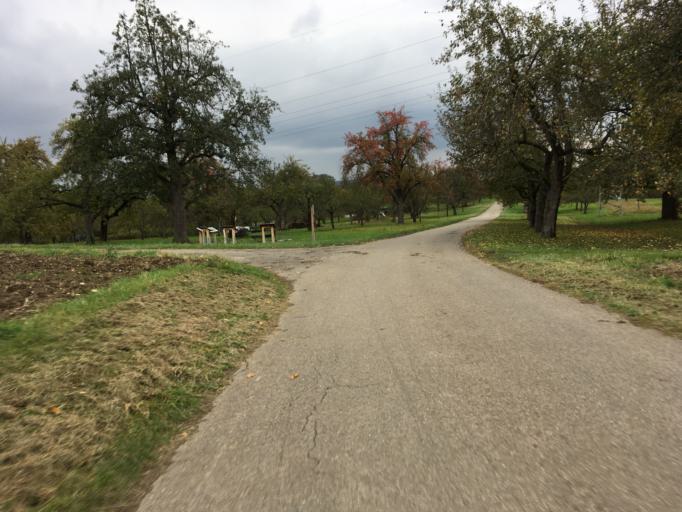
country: DE
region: Baden-Wuerttemberg
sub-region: Tuebingen Region
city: Gomaringen
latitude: 48.4426
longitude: 9.0956
